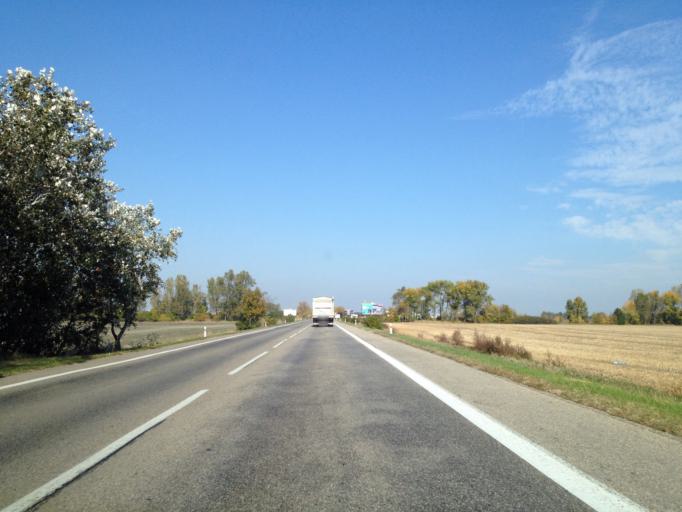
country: SK
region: Nitriansky
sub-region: Okres Nove Zamky
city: Nove Zamky
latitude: 47.9485
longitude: 18.1952
